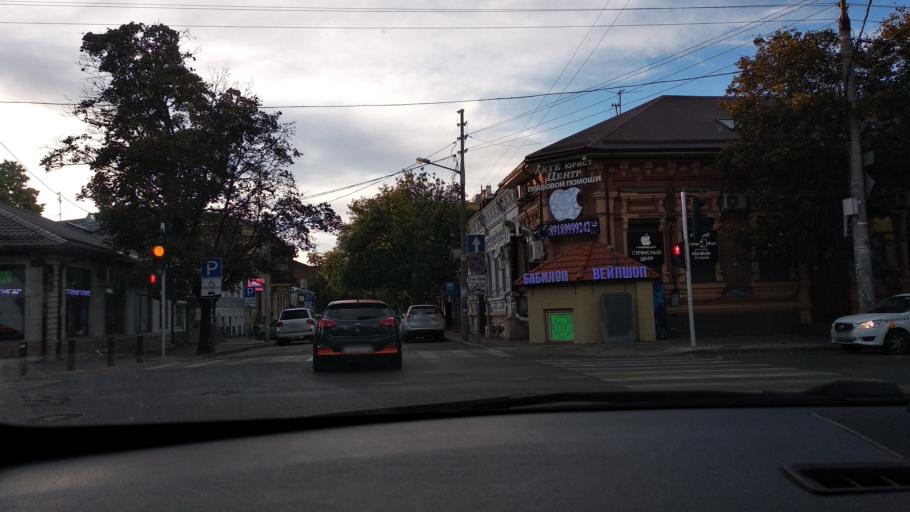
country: RU
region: Krasnodarskiy
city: Krasnodar
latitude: 45.0273
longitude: 38.9783
